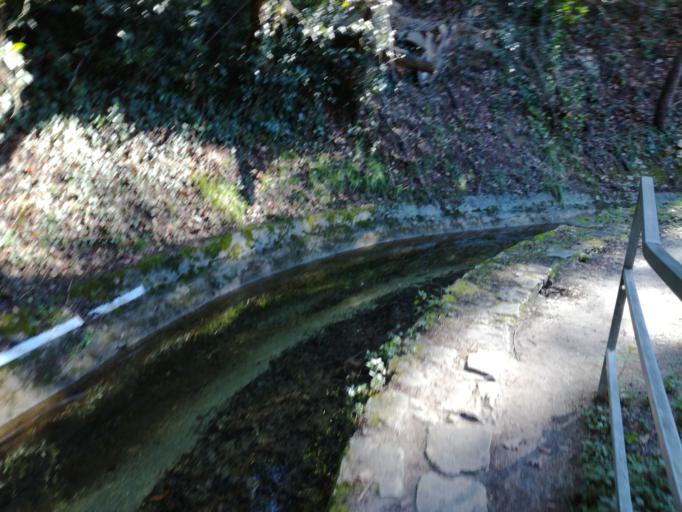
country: FR
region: Provence-Alpes-Cote d'Azur
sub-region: Departement des Alpes-Maritimes
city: Mouans-Sartoux
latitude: 43.6267
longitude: 6.9801
